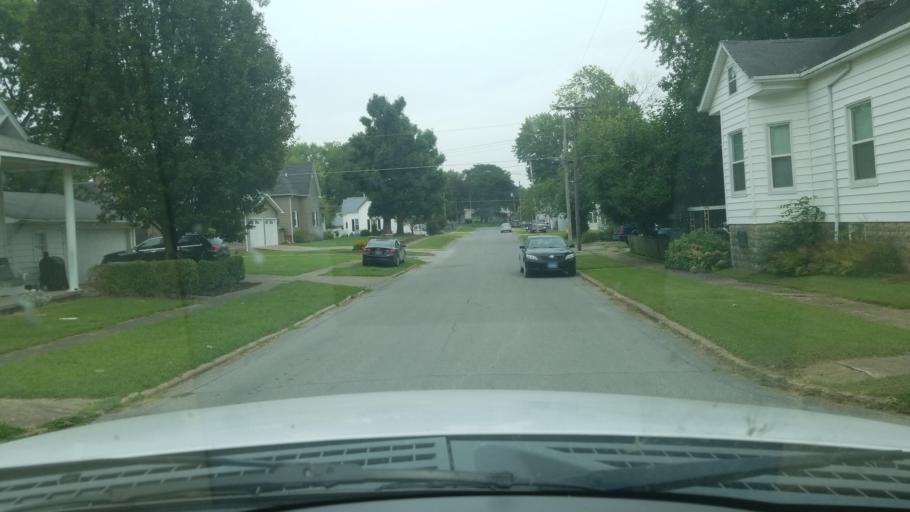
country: US
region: Illinois
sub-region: Saline County
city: Eldorado
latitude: 37.8177
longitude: -88.4415
